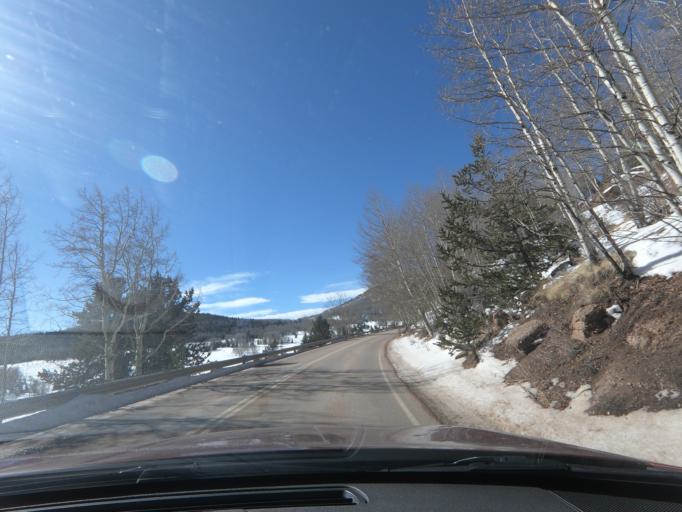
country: US
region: Colorado
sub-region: Teller County
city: Cripple Creek
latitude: 38.7421
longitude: -105.1080
